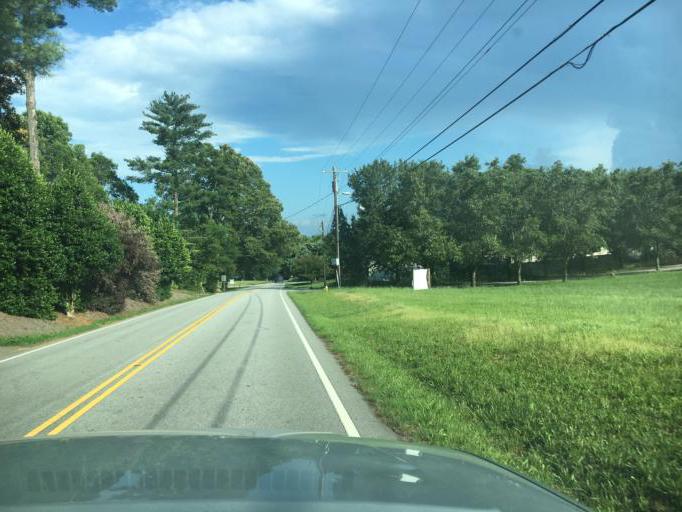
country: US
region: South Carolina
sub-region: Greenville County
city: Mauldin
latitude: 34.7773
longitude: -82.2723
